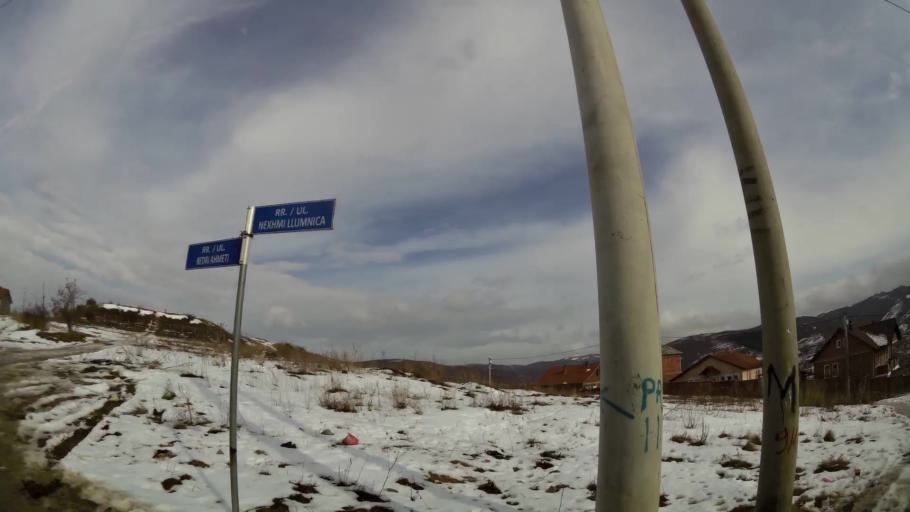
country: XK
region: Pristina
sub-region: Komuna e Prishtines
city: Pristina
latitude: 42.6853
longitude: 21.1694
